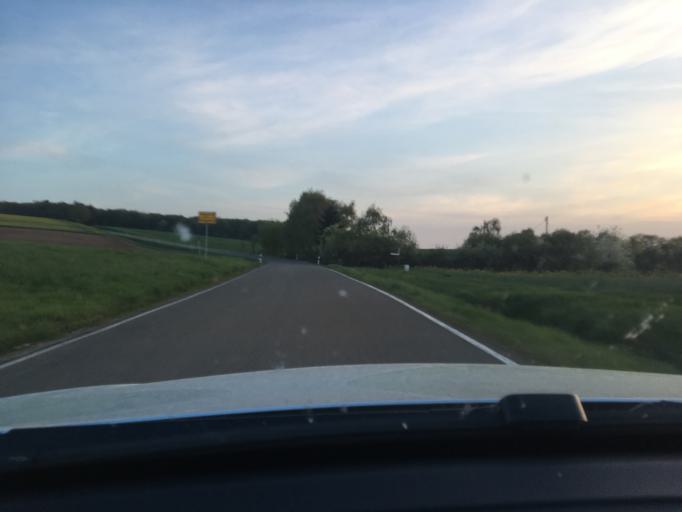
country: DE
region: Rheinland-Pfalz
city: Kriegsfeld
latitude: 49.7069
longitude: 7.9140
